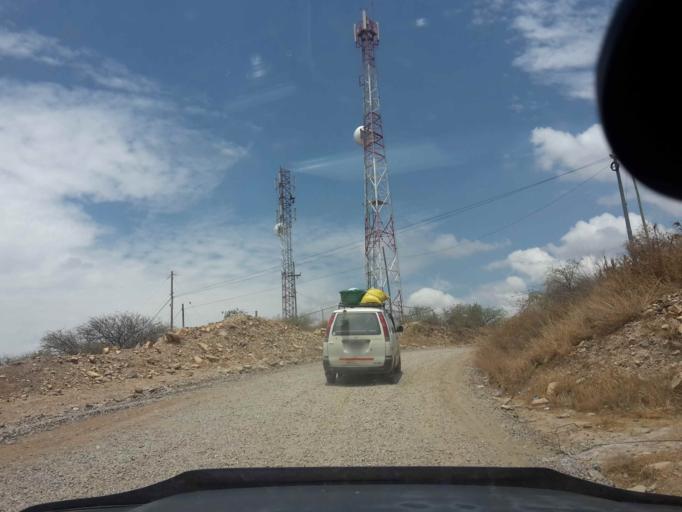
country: BO
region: Cochabamba
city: Sipe Sipe
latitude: -17.5699
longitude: -66.3488
